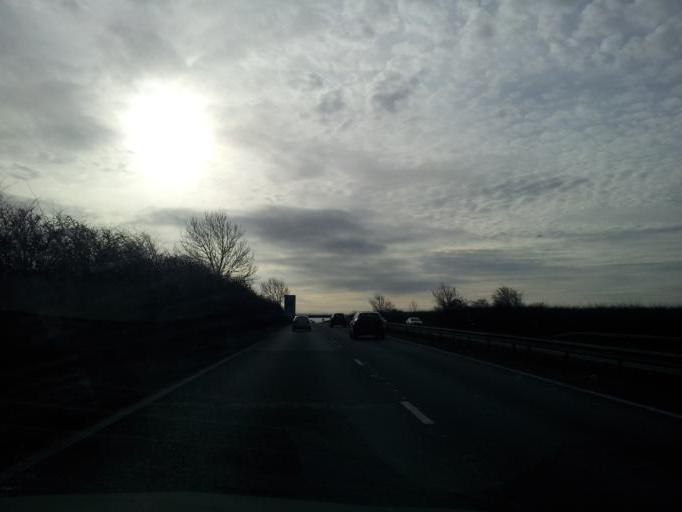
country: GB
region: England
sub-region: Lincolnshire
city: Stamford
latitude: 52.6347
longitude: -0.4772
